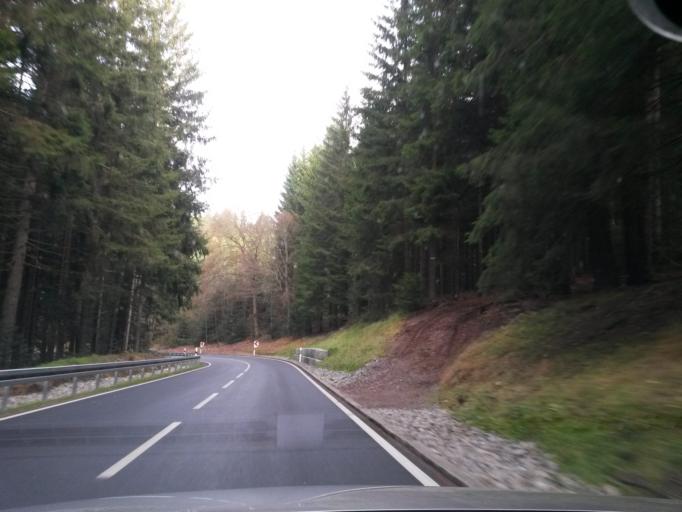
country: DE
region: Baden-Wuerttemberg
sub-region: Freiburg Region
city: Sankt Georgen im Schwarzwald
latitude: 48.1511
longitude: 8.3306
